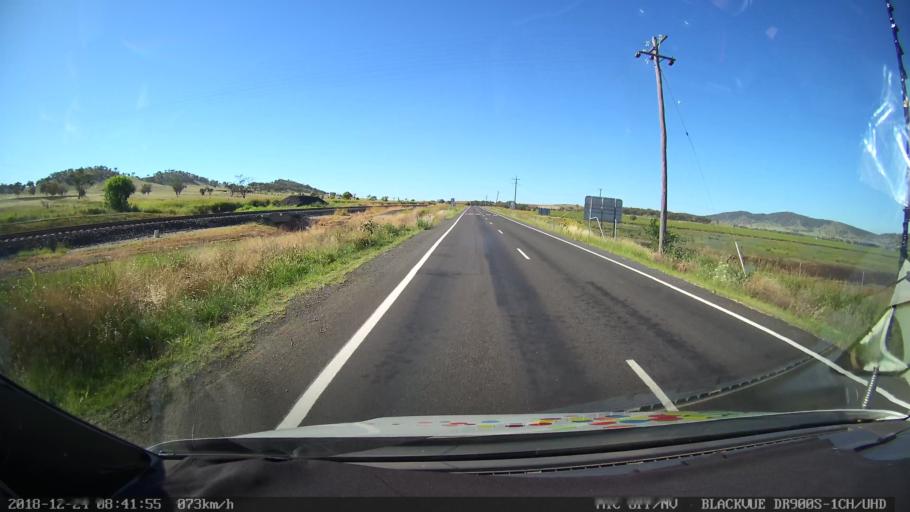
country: AU
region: New South Wales
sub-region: Liverpool Plains
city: Quirindi
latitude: -31.3676
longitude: 150.6440
